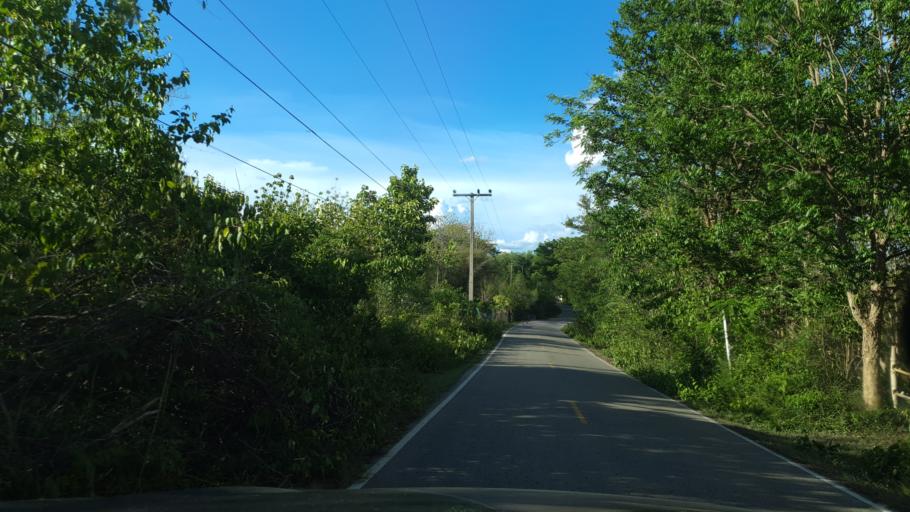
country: TH
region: Lampang
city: Sop Prap
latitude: 17.8797
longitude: 99.3104
